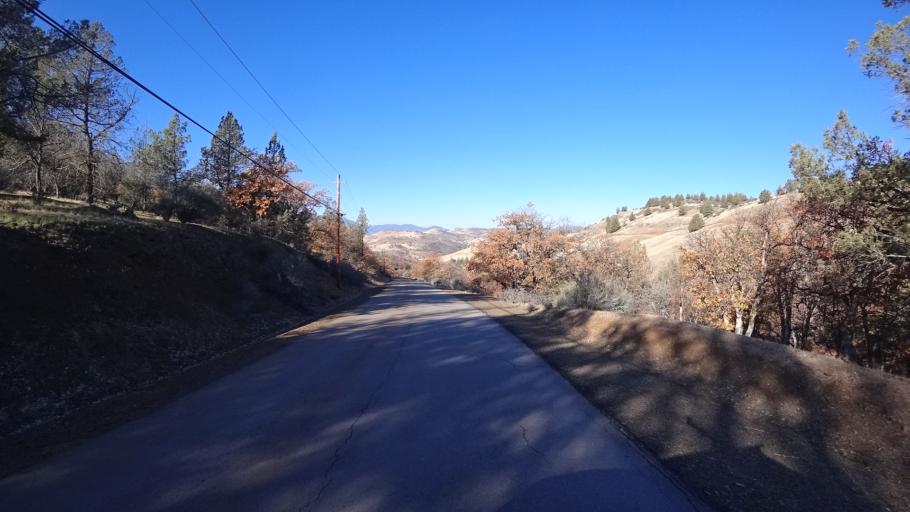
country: US
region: California
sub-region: Siskiyou County
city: Montague
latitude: 41.9149
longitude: -122.4352
